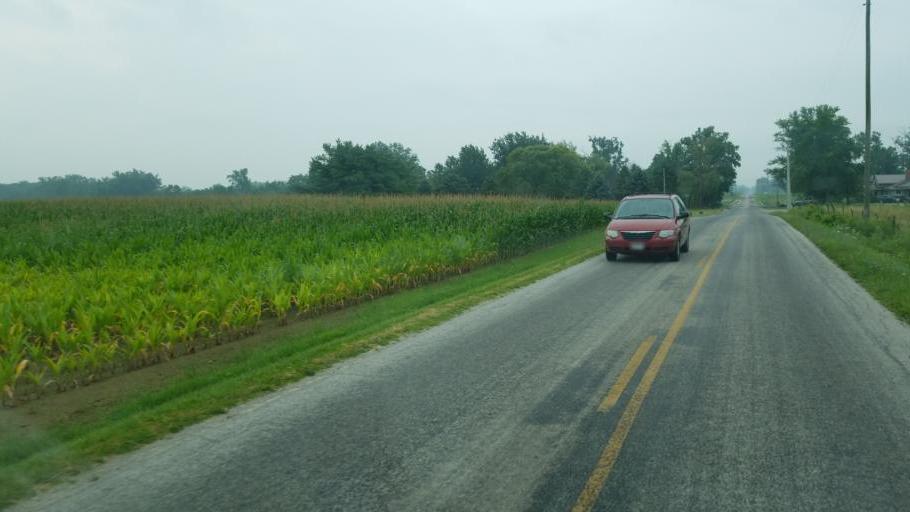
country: US
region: Ohio
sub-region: Union County
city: Richwood
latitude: 40.5612
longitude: -83.3921
